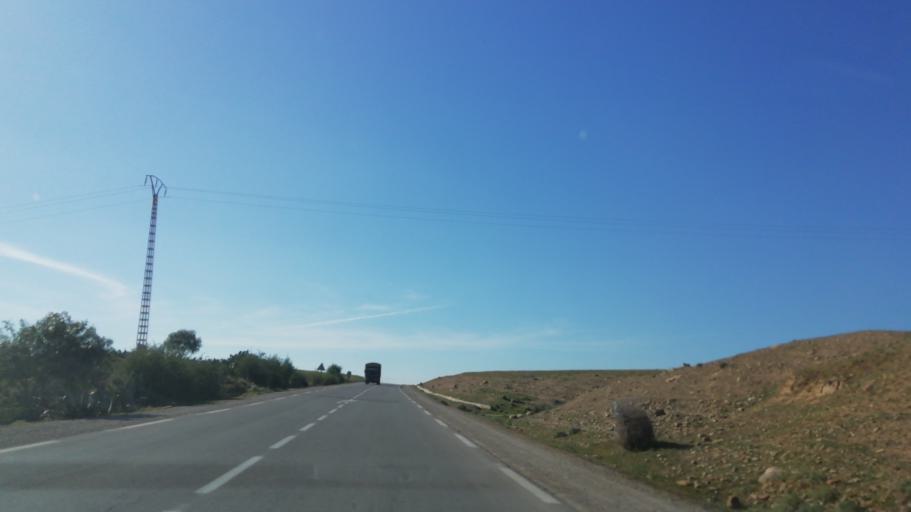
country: DZ
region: Mascara
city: Oued el Abtal
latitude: 35.4539
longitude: 0.7723
